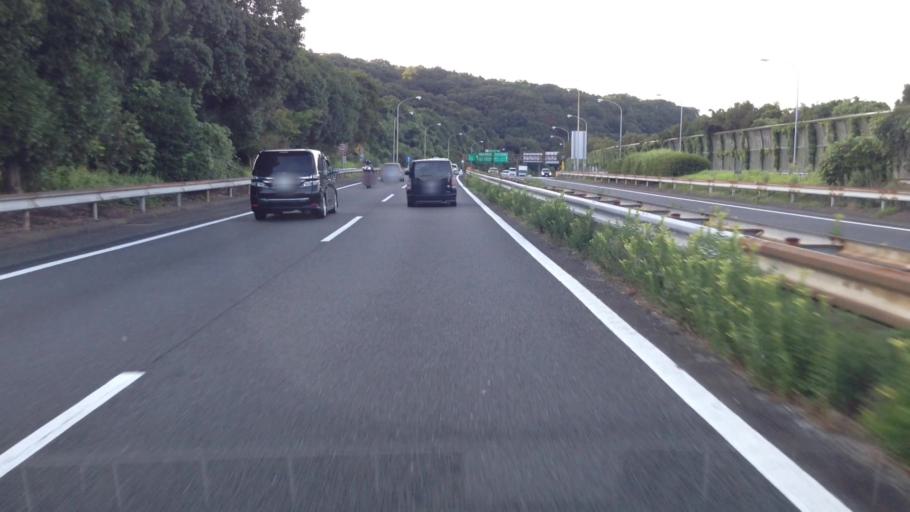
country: JP
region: Kanagawa
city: Zushi
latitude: 35.3358
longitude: 139.5914
